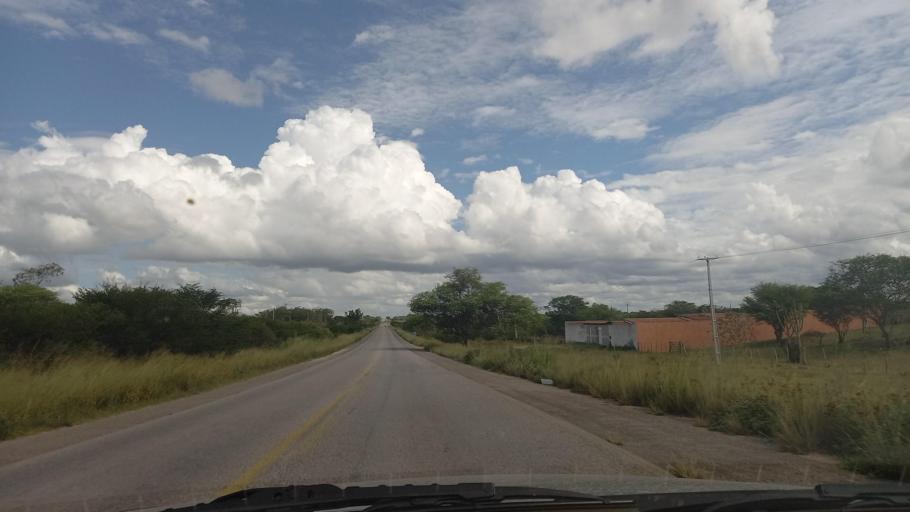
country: BR
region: Pernambuco
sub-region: Cachoeirinha
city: Cachoeirinha
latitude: -8.4483
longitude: -36.2101
